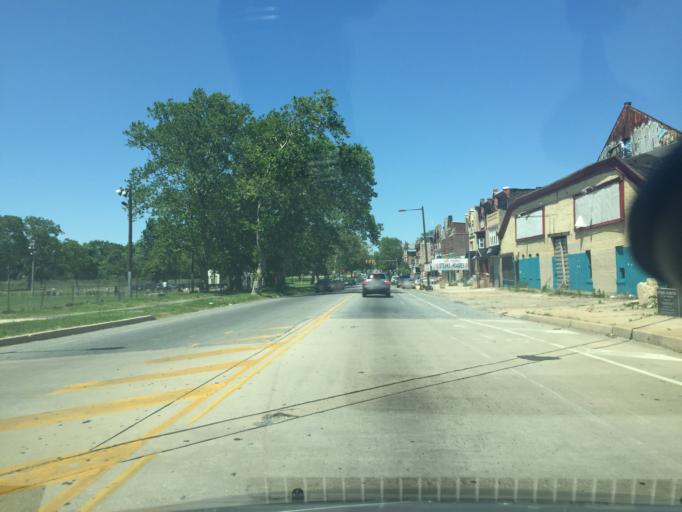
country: US
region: Pennsylvania
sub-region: Philadelphia County
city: Philadelphia
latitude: 39.9796
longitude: -75.1890
